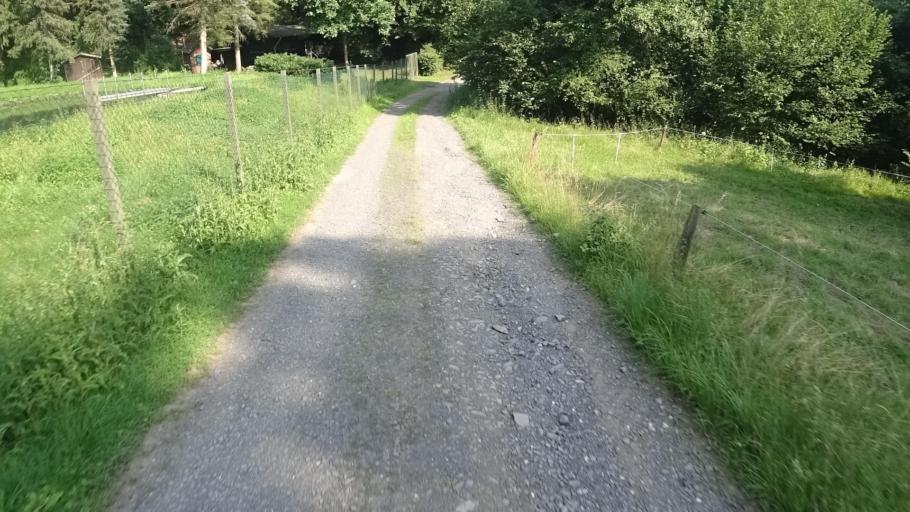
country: DE
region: Rheinland-Pfalz
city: Sankt Katharinen
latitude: 50.5584
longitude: 7.3658
